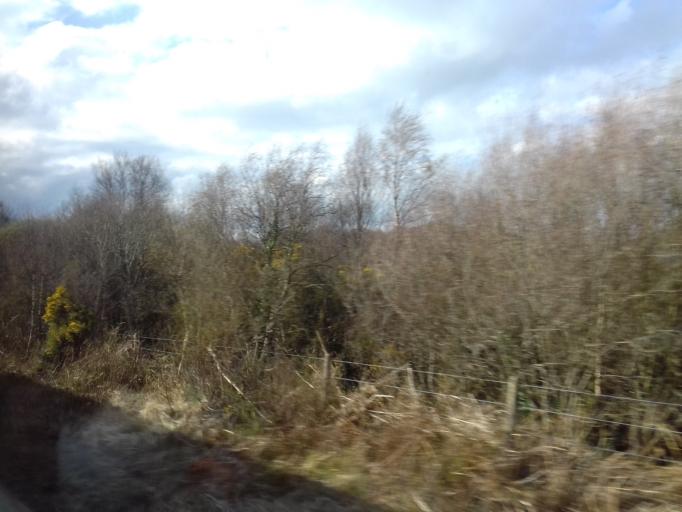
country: IE
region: Leinster
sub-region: An Iarmhi
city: Kinnegad
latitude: 53.4771
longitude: -7.0508
